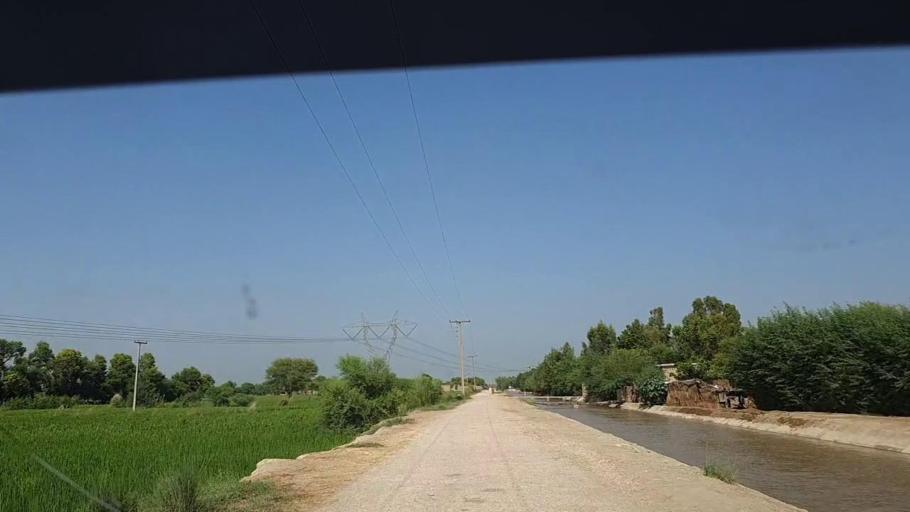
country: PK
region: Sindh
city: Ghauspur
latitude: 28.1528
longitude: 69.0826
